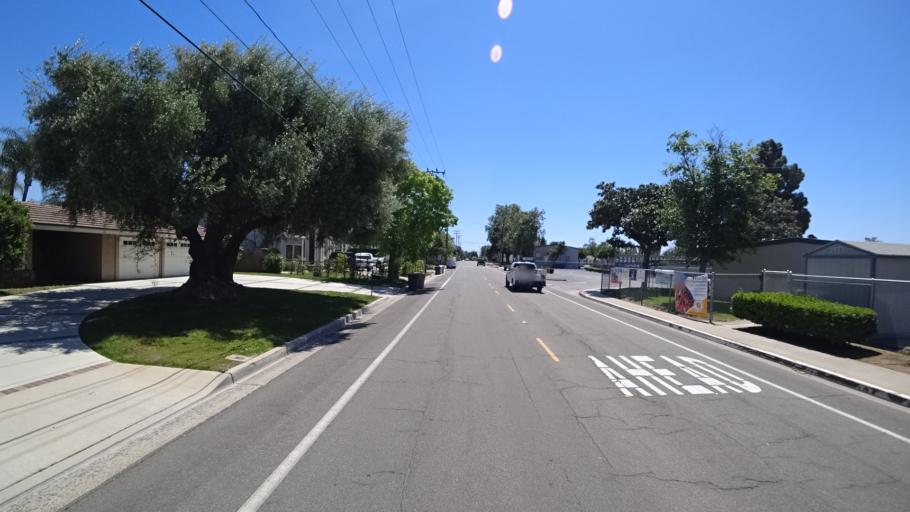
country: US
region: California
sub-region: Orange County
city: Villa Park
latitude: 33.8091
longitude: -117.8133
